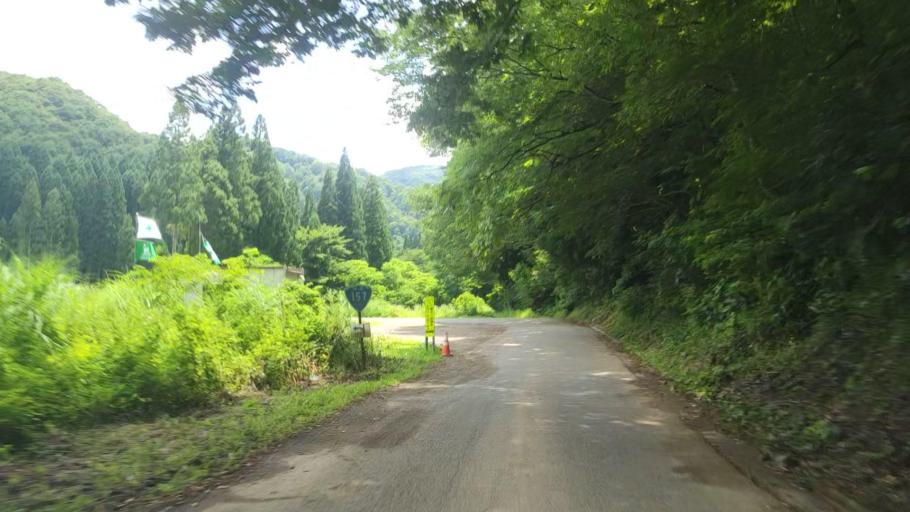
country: JP
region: Fukui
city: Ono
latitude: 35.8204
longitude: 136.4512
